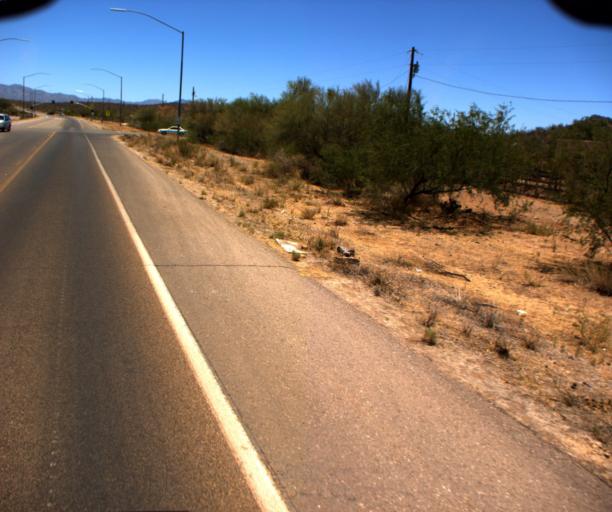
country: US
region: Arizona
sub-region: Pima County
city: Sells
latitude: 31.9164
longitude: -111.8667
